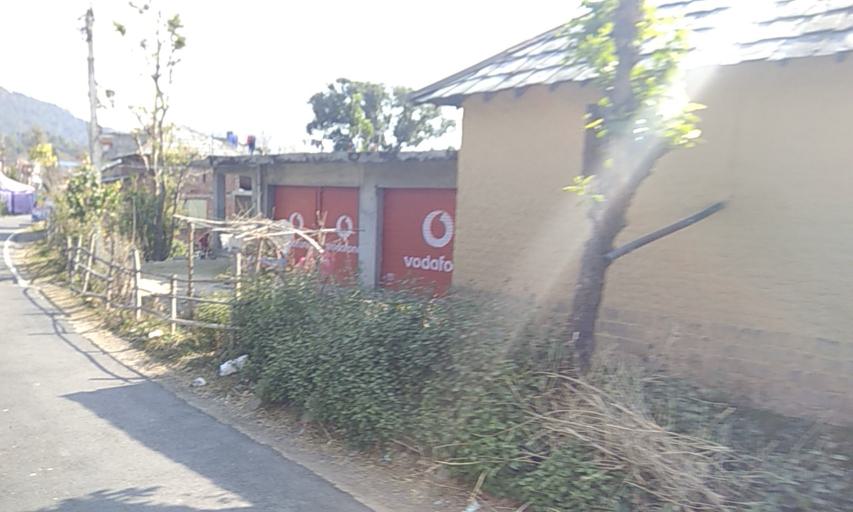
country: IN
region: Himachal Pradesh
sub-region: Kangra
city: Dharmsala
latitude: 32.1562
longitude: 76.4145
